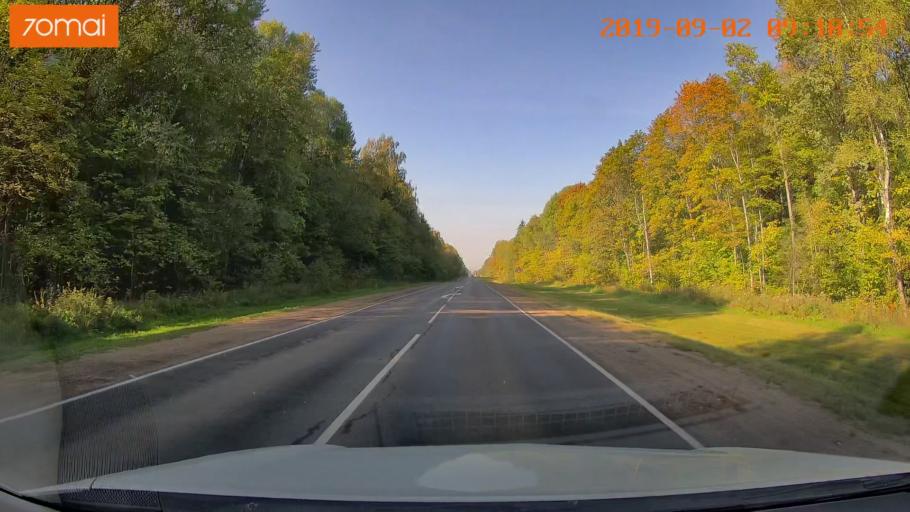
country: RU
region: Kaluga
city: Myatlevo
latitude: 54.8721
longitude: 35.5892
